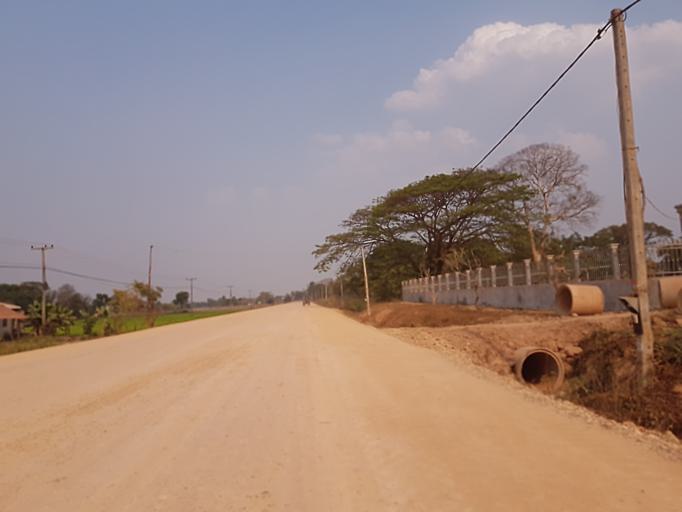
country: TH
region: Nong Khai
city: Nong Khai
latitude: 17.9808
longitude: 102.8811
